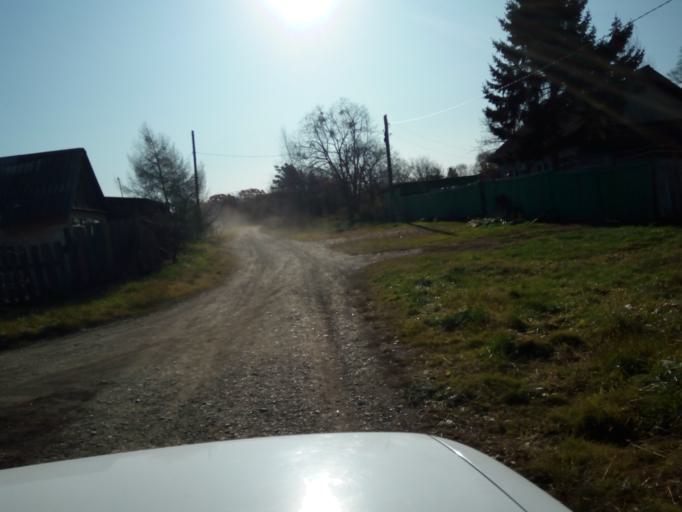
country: RU
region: Primorskiy
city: Lazo
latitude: 45.8725
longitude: 133.6498
